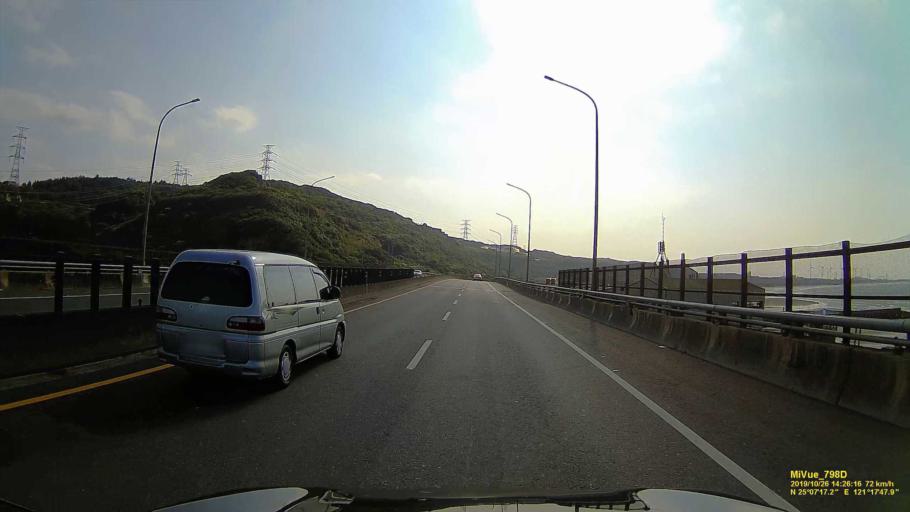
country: TW
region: Taiwan
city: Taoyuan City
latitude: 25.1221
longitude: 121.2975
